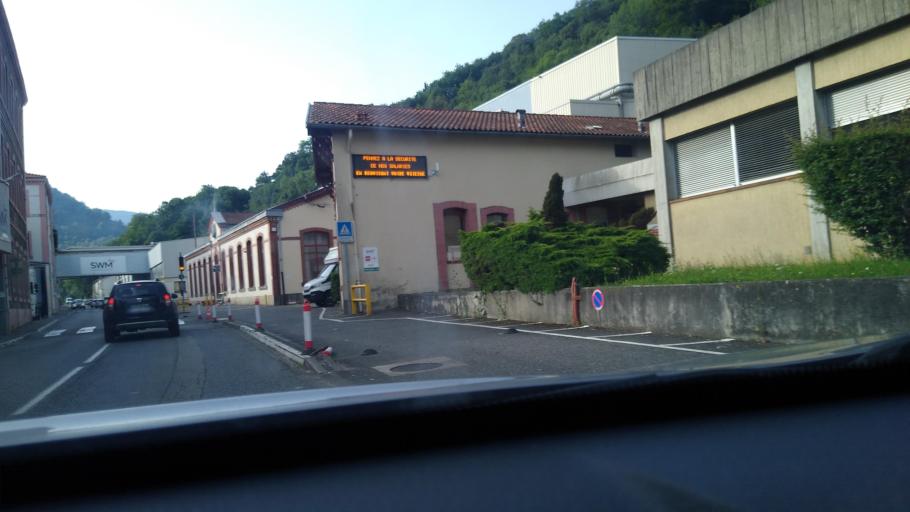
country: FR
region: Midi-Pyrenees
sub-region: Departement de l'Ariege
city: Saint-Girons
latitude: 42.9648
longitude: 1.1699
